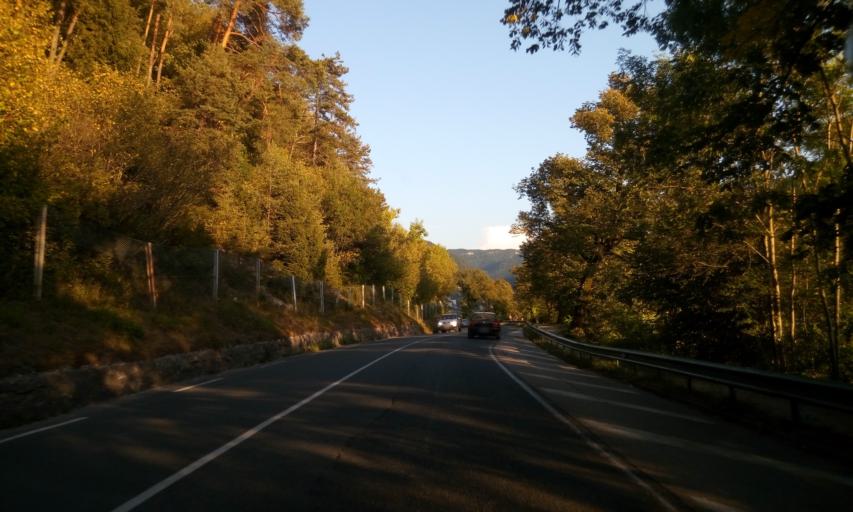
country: FR
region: Rhone-Alpes
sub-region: Departement de l'Ain
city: Montreal-la-Cluse
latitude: 46.1659
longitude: 5.5829
